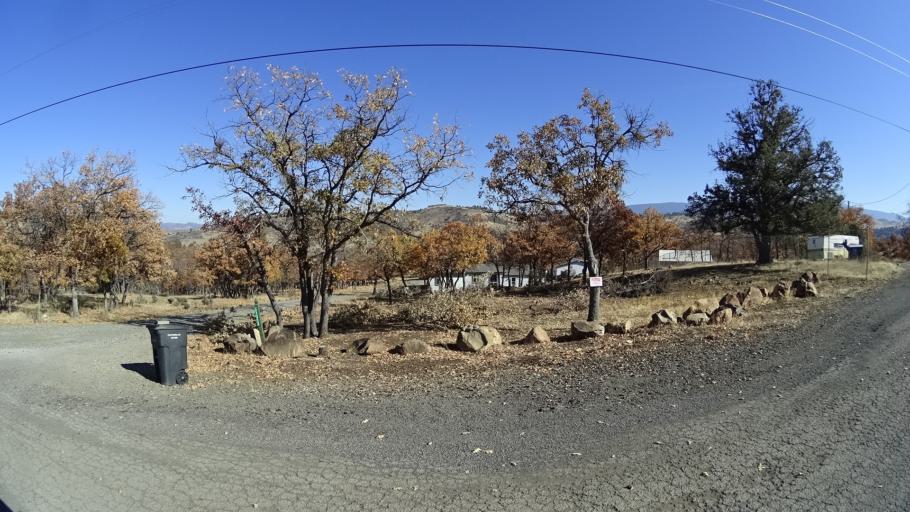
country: US
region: California
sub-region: Siskiyou County
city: Montague
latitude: 41.8735
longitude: -122.4837
